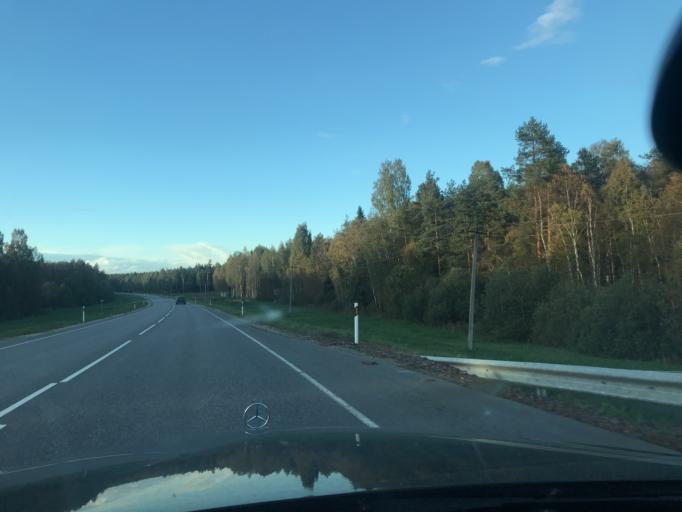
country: EE
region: Vorumaa
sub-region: Voru linn
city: Voru
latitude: 57.8295
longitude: 27.0630
